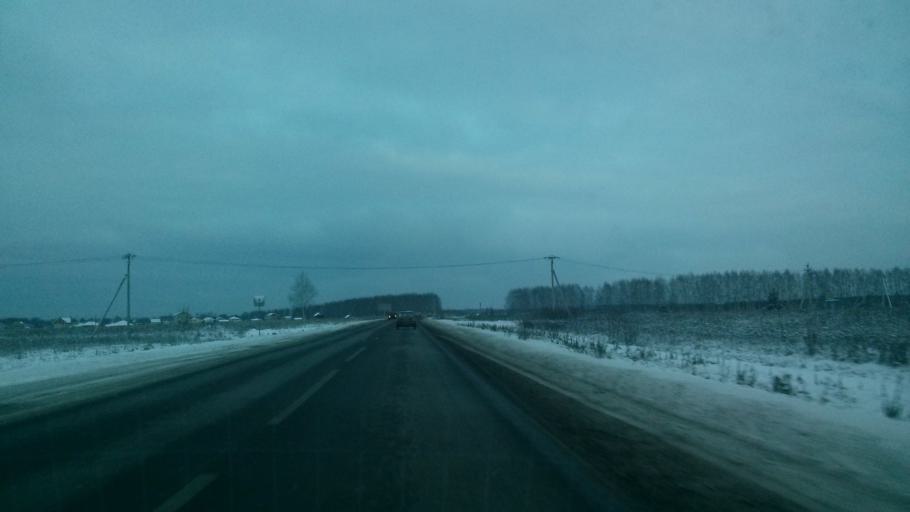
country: RU
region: Nizjnij Novgorod
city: Bogorodsk
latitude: 56.0831
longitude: 43.4812
